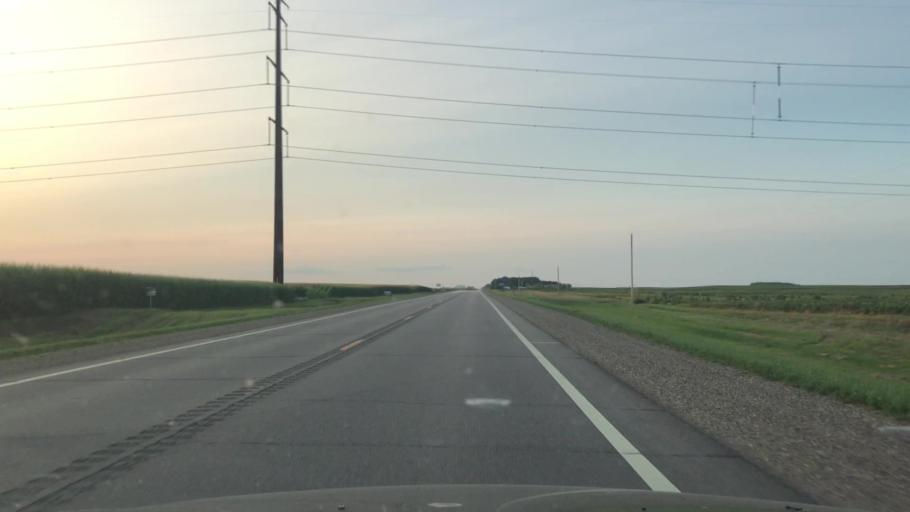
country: US
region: Minnesota
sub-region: Redwood County
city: Redwood Falls
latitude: 44.4334
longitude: -95.1176
